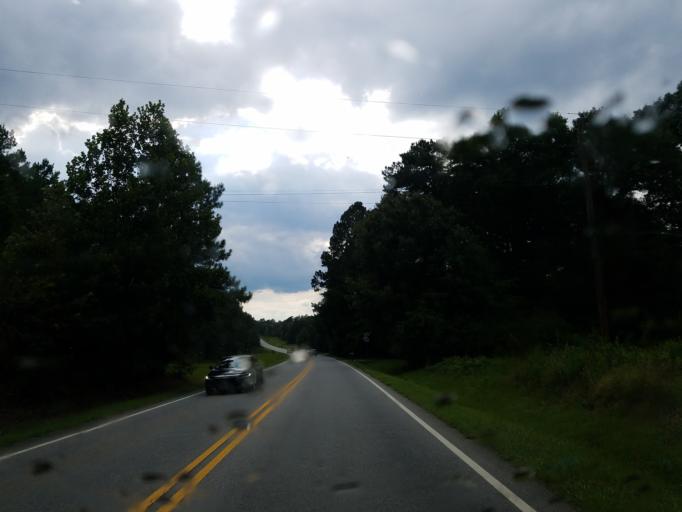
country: US
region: Georgia
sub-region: Floyd County
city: Shannon
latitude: 34.3688
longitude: -85.0831
